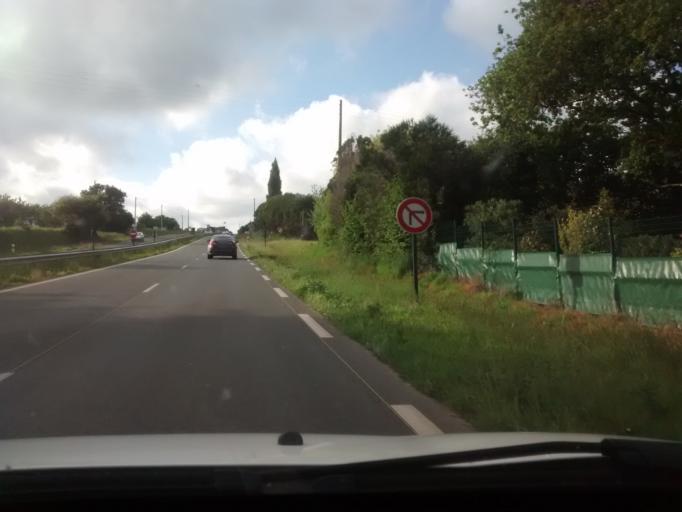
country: FR
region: Brittany
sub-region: Departement des Cotes-d'Armor
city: Saint-Quay-Perros
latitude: 48.7765
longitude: -3.4469
